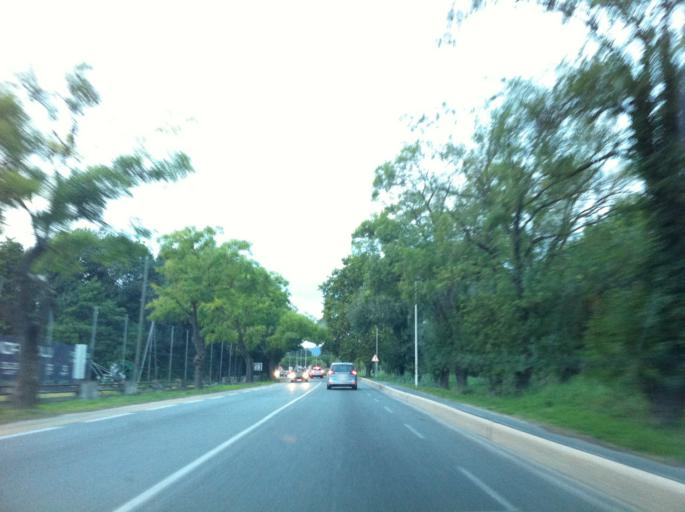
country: FR
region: Provence-Alpes-Cote d'Azur
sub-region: Departement du Var
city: Gassin
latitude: 43.2602
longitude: 6.5899
